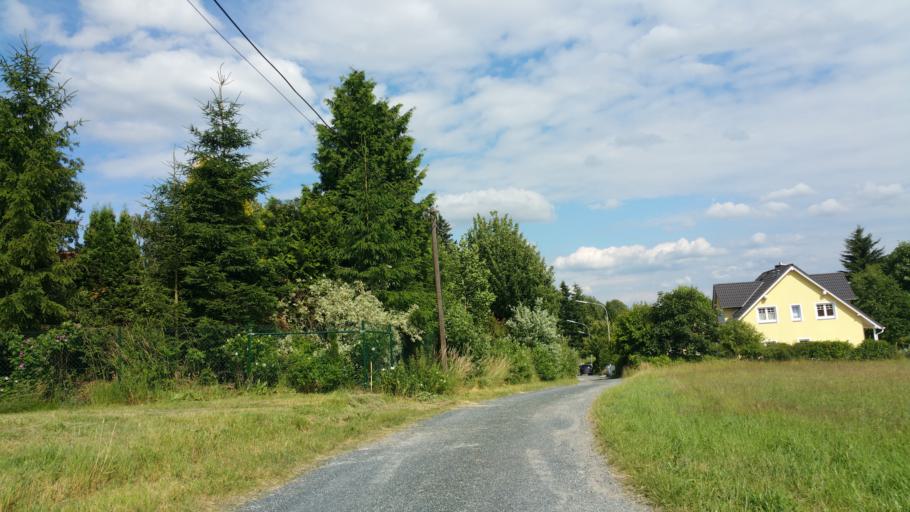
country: DE
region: Bavaria
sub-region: Upper Franconia
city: Oberkotzau
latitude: 50.2690
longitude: 11.9196
